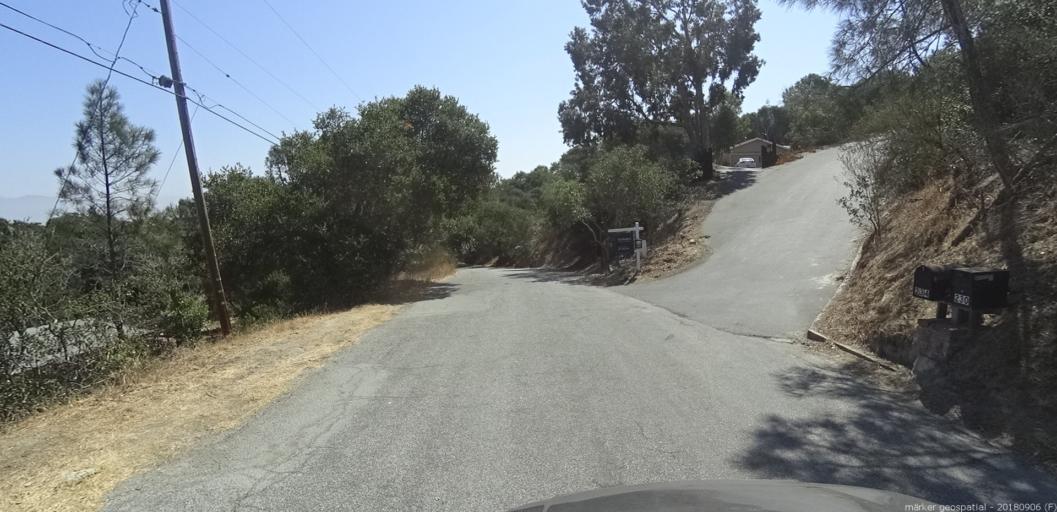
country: US
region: California
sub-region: Monterey County
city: Salinas
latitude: 36.5805
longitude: -121.6328
